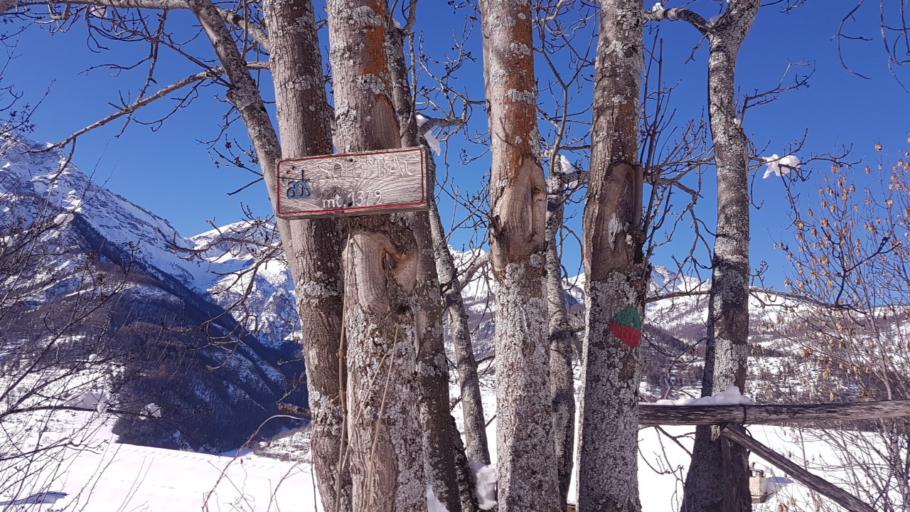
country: IT
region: Piedmont
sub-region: Provincia di Torino
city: Cesana Torinese
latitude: 44.9824
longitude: 6.8126
